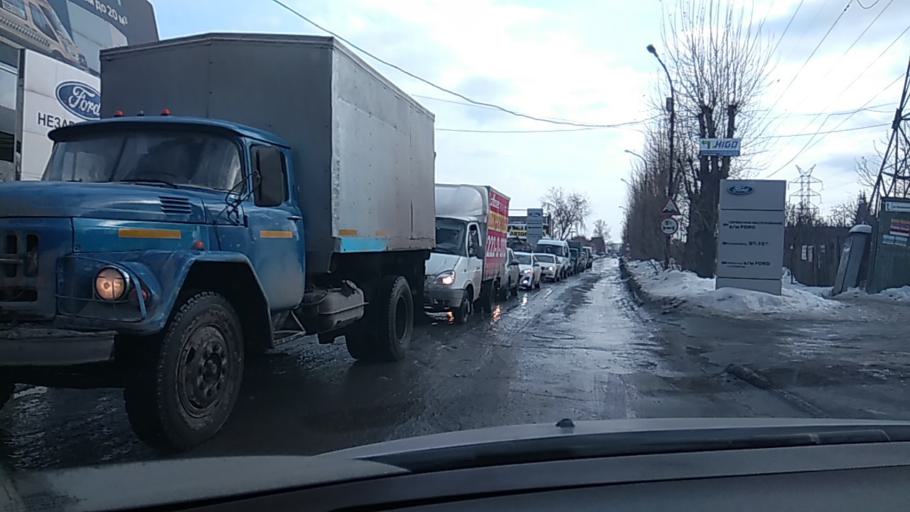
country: RU
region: Sverdlovsk
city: Yekaterinburg
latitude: 56.8619
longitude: 60.6636
